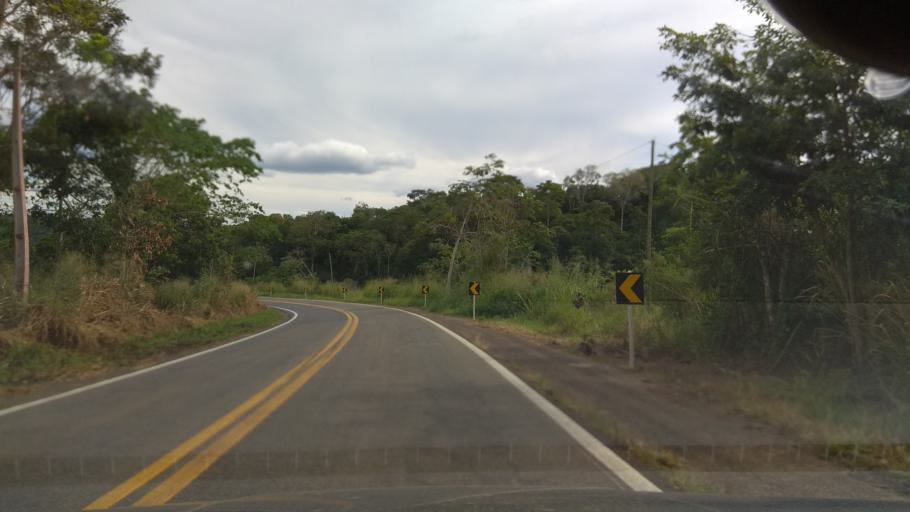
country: BR
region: Bahia
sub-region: Ubata
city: Ubata
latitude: -14.2029
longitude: -39.5728
